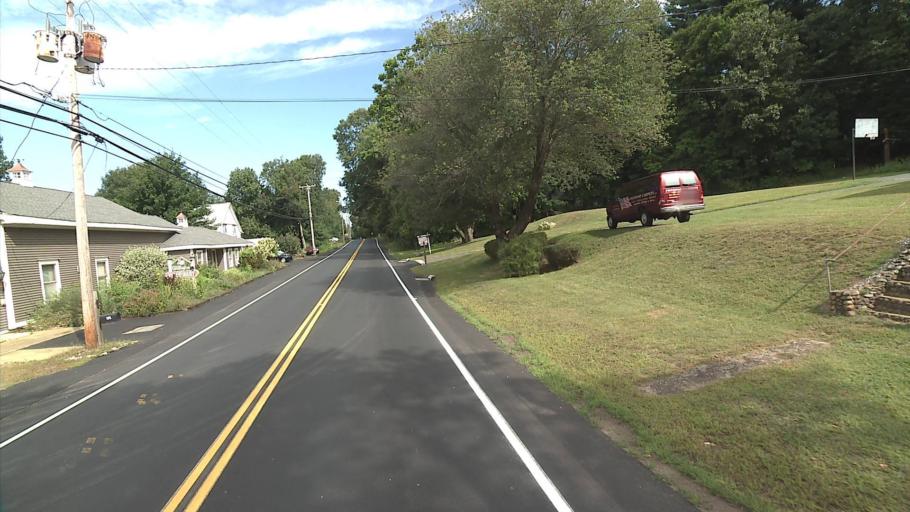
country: US
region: Connecticut
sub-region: Tolland County
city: Tolland
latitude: 41.8618
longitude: -72.3018
